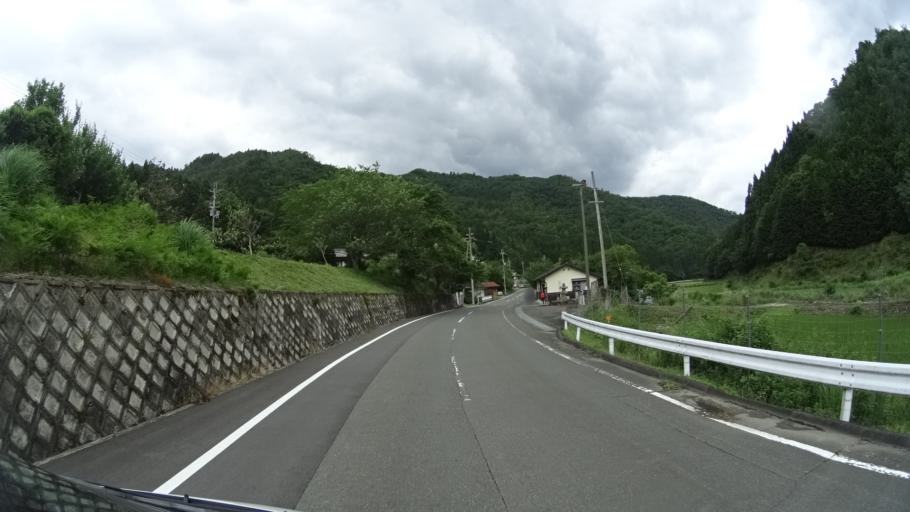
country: JP
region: Hyogo
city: Sasayama
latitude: 35.0556
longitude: 135.3957
